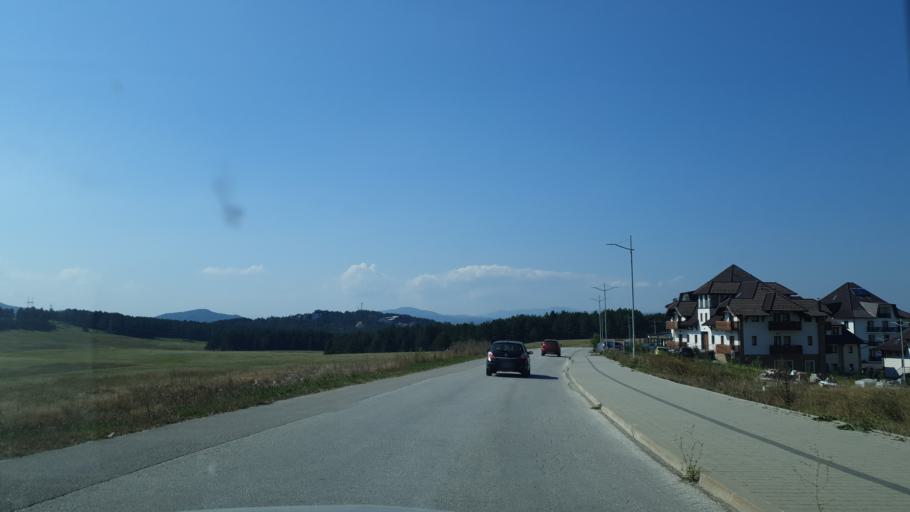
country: RS
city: Zlatibor
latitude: 43.7174
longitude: 19.7167
